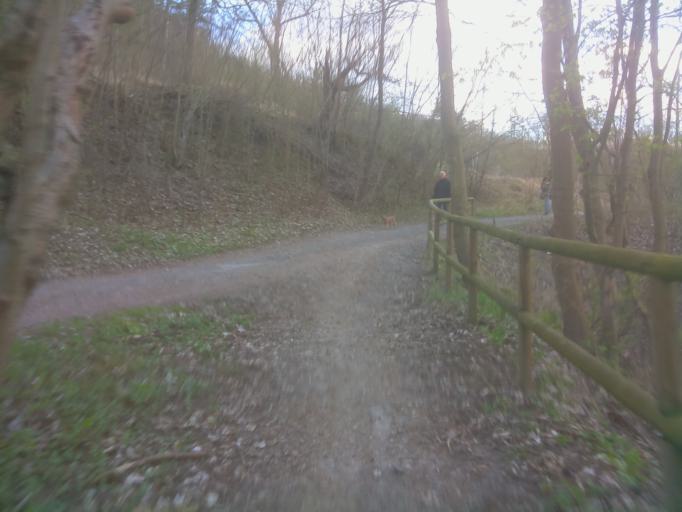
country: DE
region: Thuringia
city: Grosspurschutz
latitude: 50.8073
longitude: 11.5962
